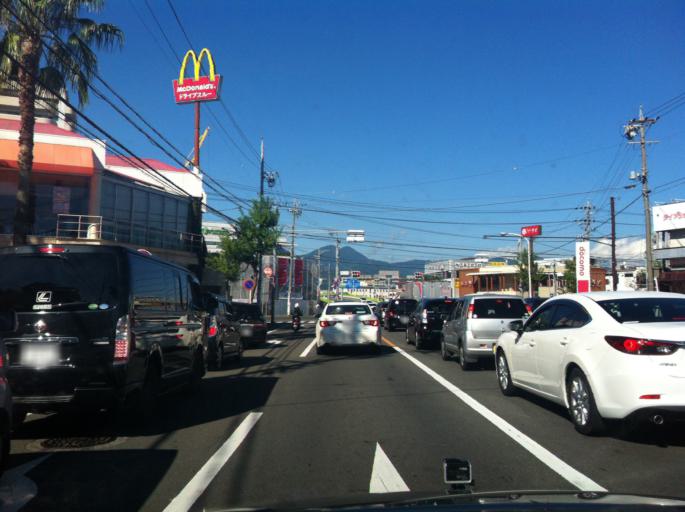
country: JP
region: Shizuoka
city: Shizuoka-shi
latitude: 34.9852
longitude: 138.4225
